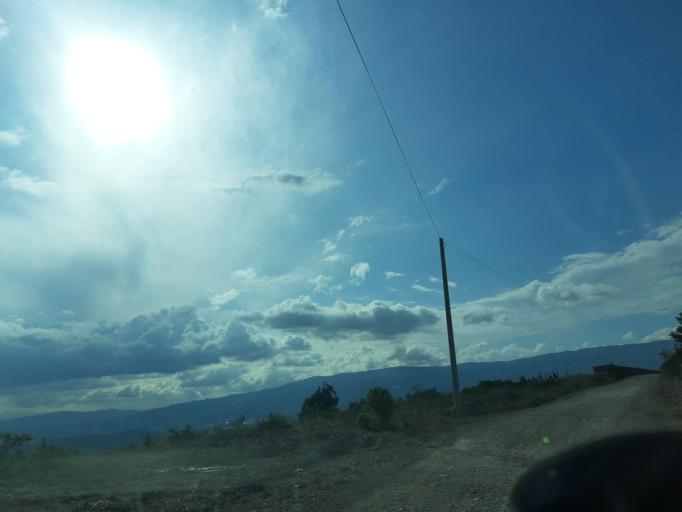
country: CO
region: Boyaca
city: Villa de Leiva
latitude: 5.6600
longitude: -73.5488
